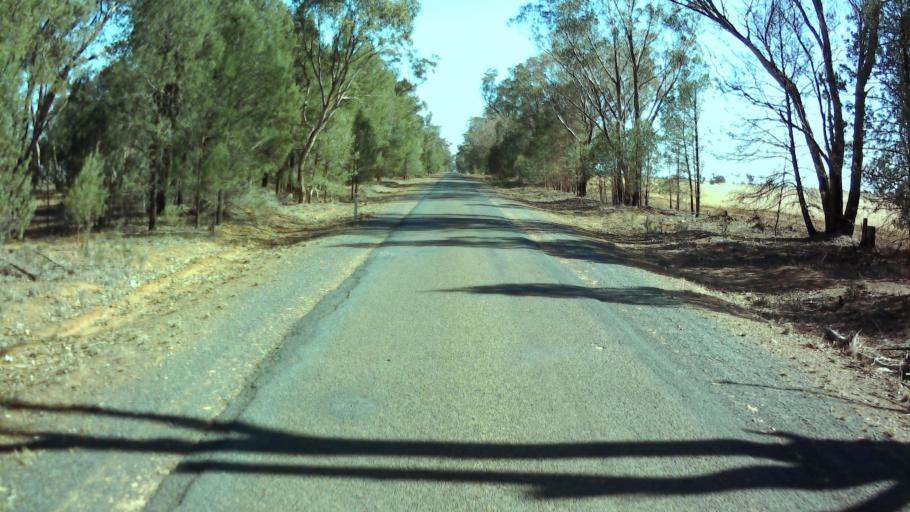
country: AU
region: New South Wales
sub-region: Weddin
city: Grenfell
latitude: -33.8099
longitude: 147.9542
